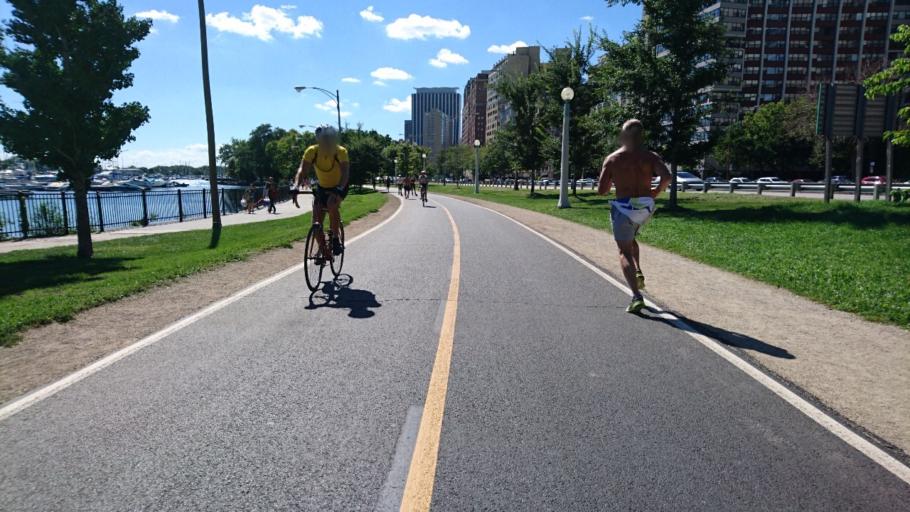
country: US
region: Illinois
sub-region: Cook County
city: Chicago
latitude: 41.9452
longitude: -87.6407
